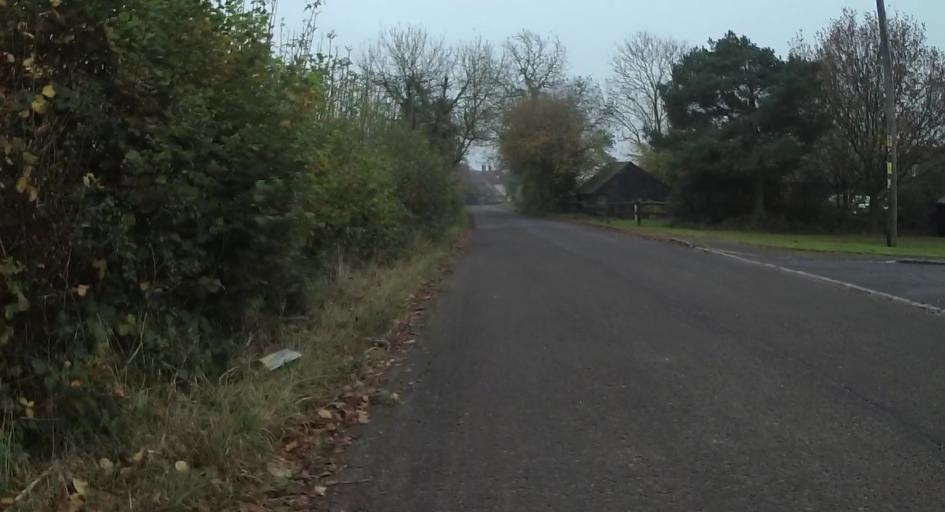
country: GB
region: England
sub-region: Hampshire
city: Old Basing
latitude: 51.2003
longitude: -1.0397
